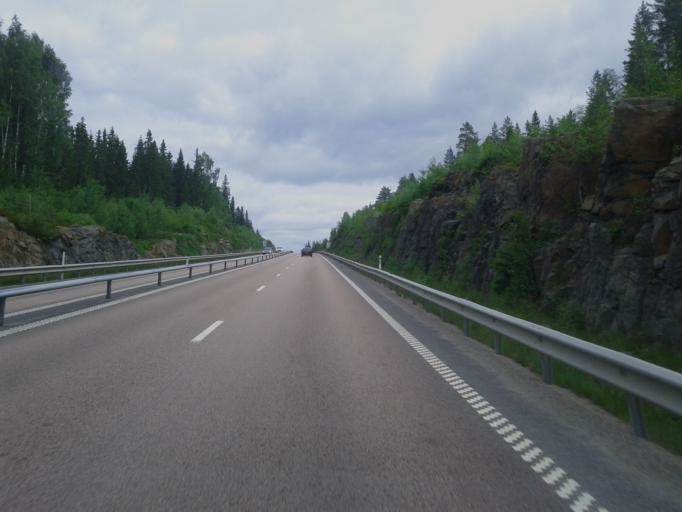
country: SE
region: Vaesternorrland
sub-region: OErnskoeldsviks Kommun
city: Bjasta
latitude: 63.1819
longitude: 18.4510
